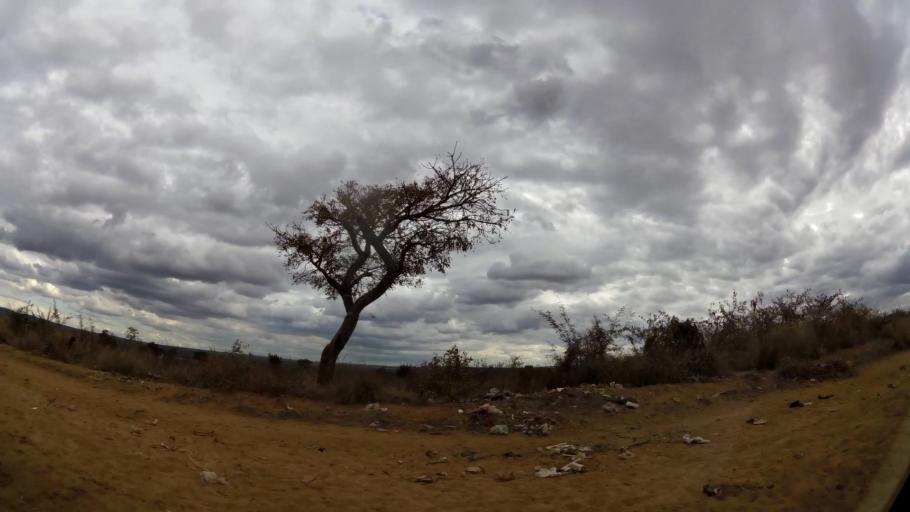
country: ZA
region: Limpopo
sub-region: Waterberg District Municipality
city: Modimolle
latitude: -24.6931
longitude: 28.4222
